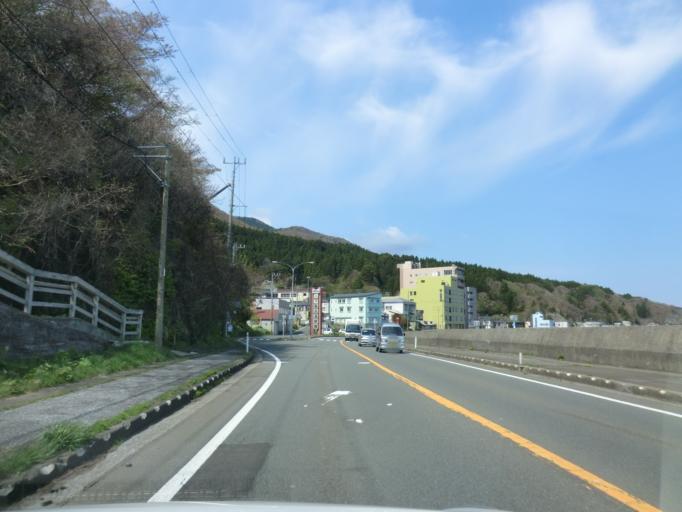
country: JP
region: Aomori
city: Mutsu
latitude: 41.4671
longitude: 141.0963
